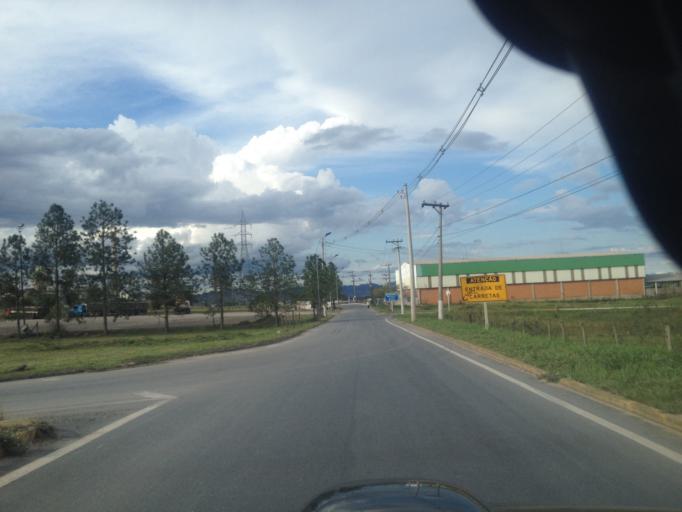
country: BR
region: Rio de Janeiro
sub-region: Porto Real
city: Porto Real
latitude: -22.4291
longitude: -44.3166
